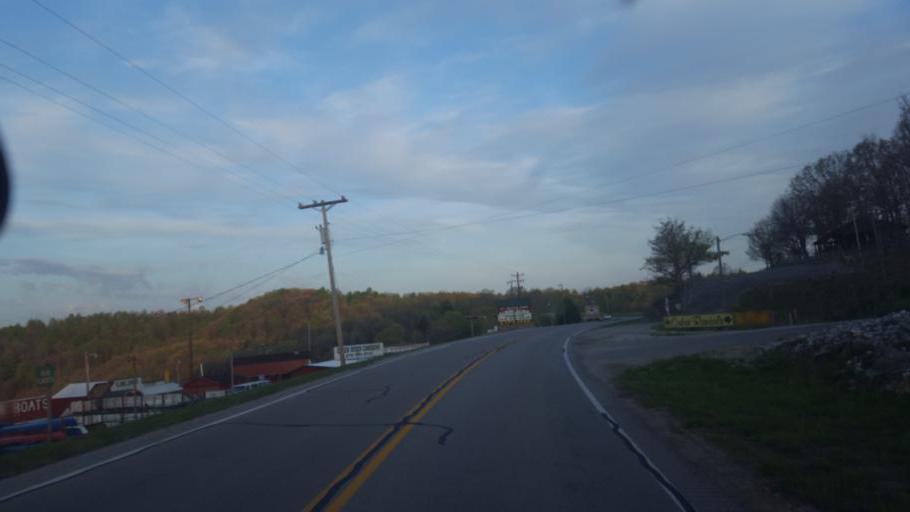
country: US
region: Kentucky
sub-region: Barren County
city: Cave City
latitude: 37.1331
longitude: -86.0034
